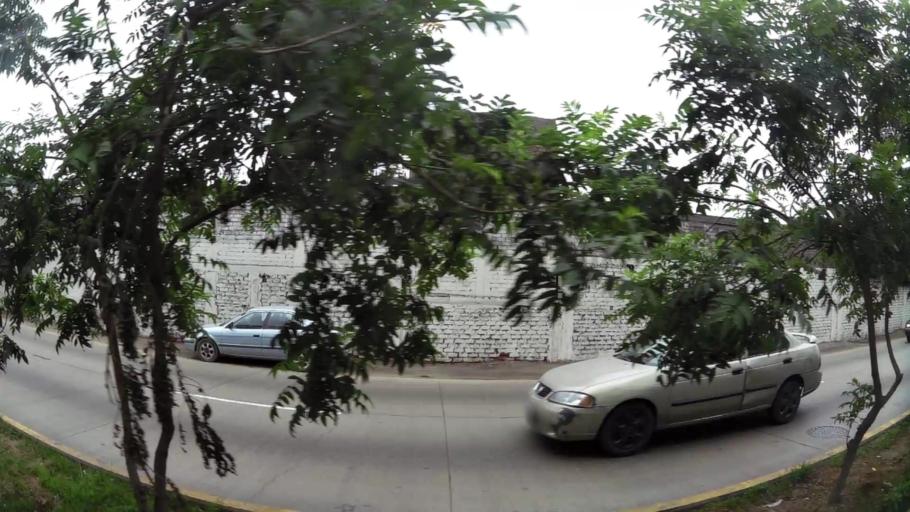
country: PE
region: Lima
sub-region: Lima
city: Surco
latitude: -12.1356
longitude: -76.9761
